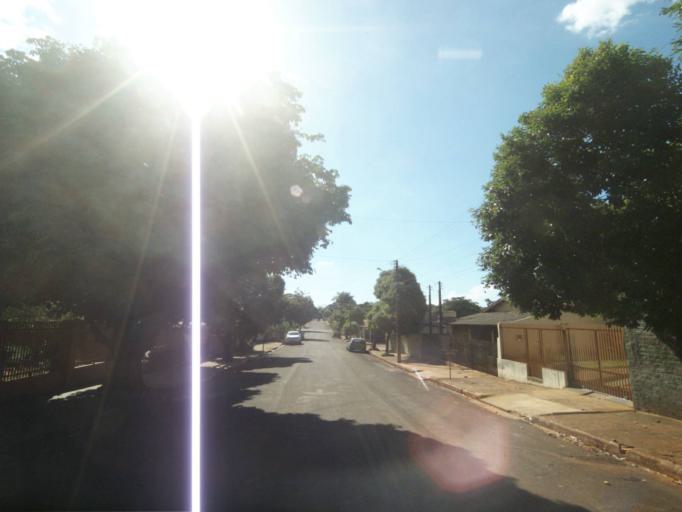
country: BR
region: Parana
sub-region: Sertanopolis
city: Sertanopolis
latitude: -23.0351
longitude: -50.8154
